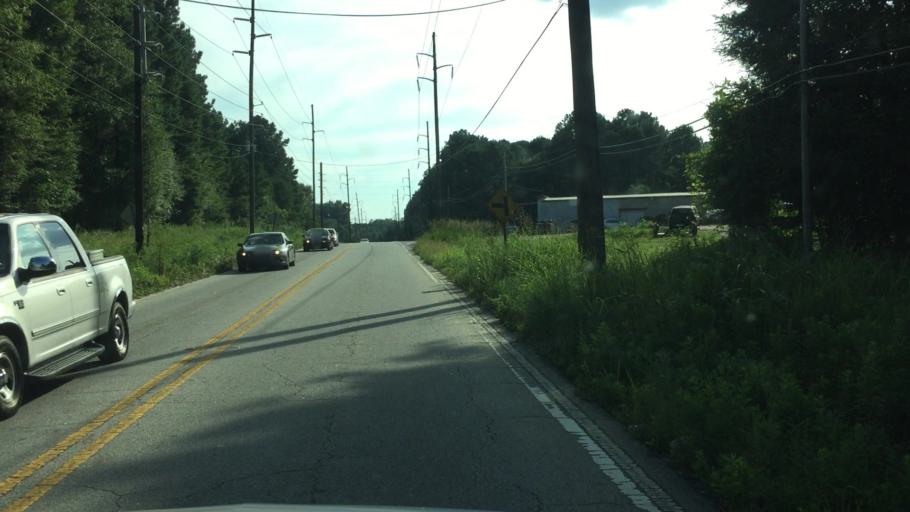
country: US
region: Georgia
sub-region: DeKalb County
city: Lithonia
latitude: 33.7221
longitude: -84.0952
